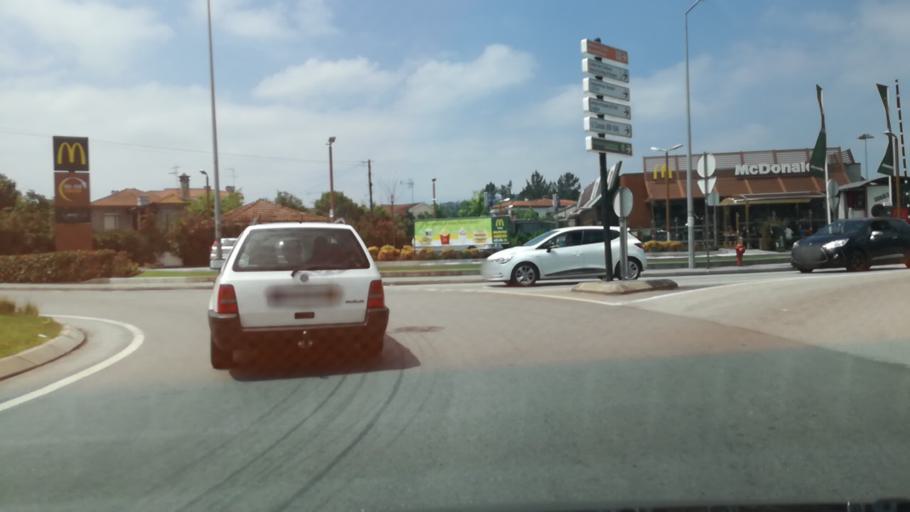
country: PT
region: Porto
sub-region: Trofa
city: Bougado
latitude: 41.3266
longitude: -8.5680
